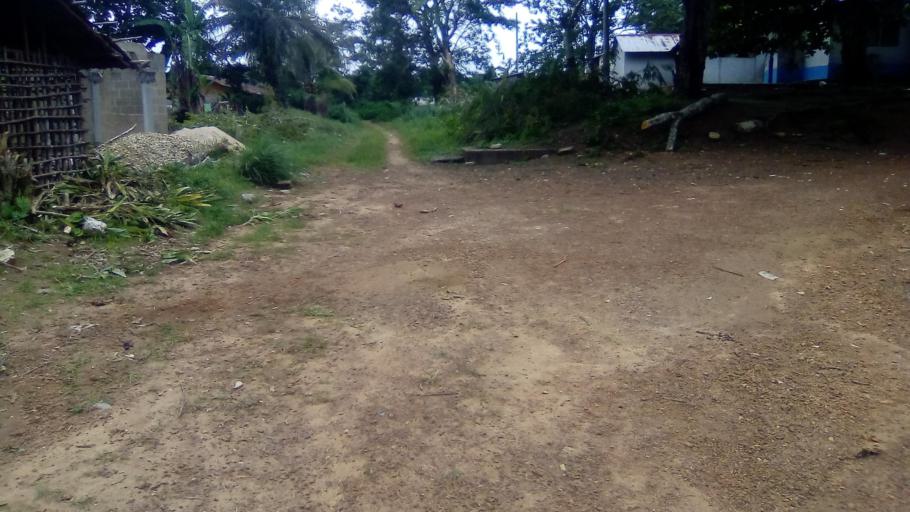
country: SL
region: Southern Province
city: Pujehun
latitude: 7.3629
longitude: -11.7079
